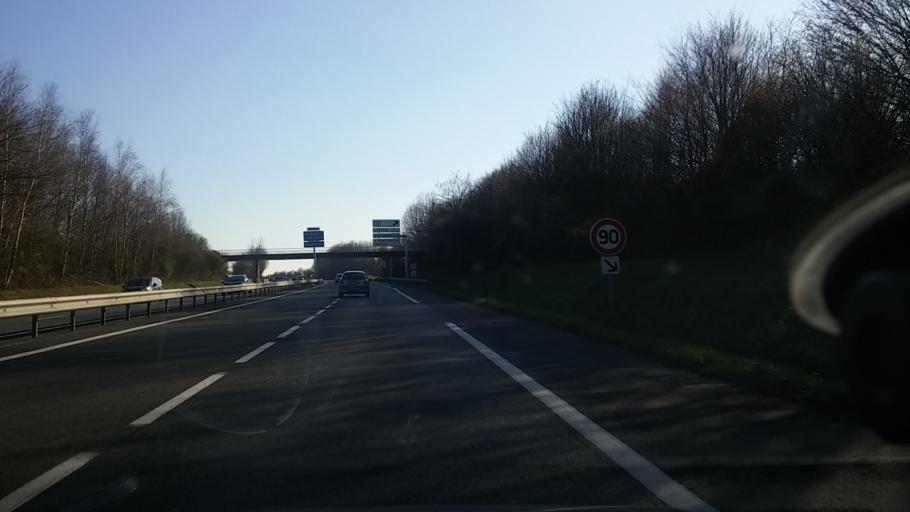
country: FR
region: Centre
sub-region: Departement de l'Indre
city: Chantome
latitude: 46.4451
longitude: 1.4851
